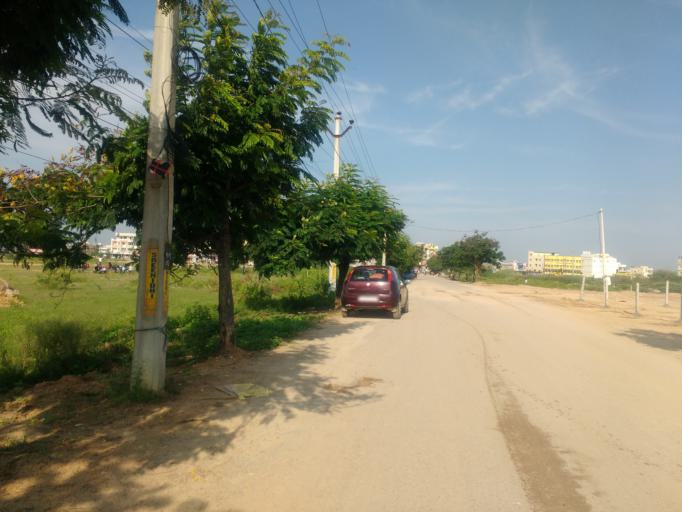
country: IN
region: Telangana
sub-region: Medak
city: Patancheru
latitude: 17.5313
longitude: 78.3011
